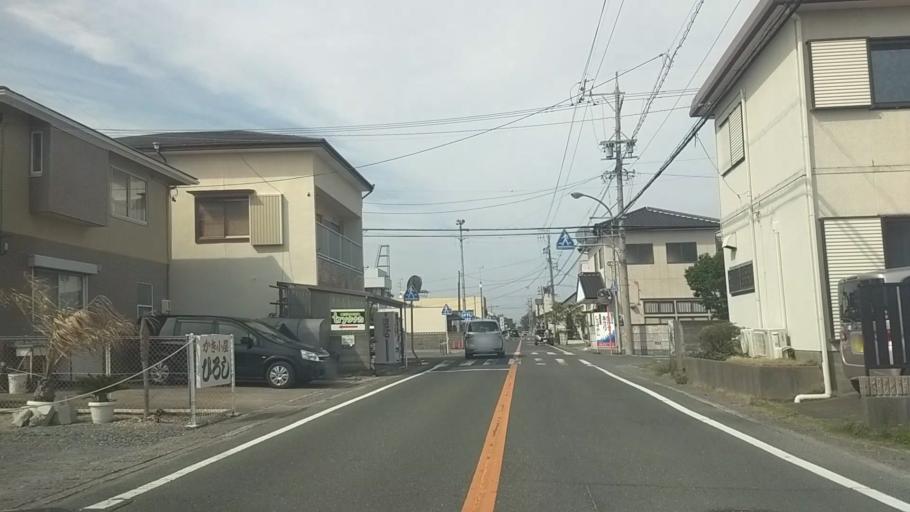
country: JP
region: Shizuoka
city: Kosai-shi
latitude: 34.6921
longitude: 137.6050
